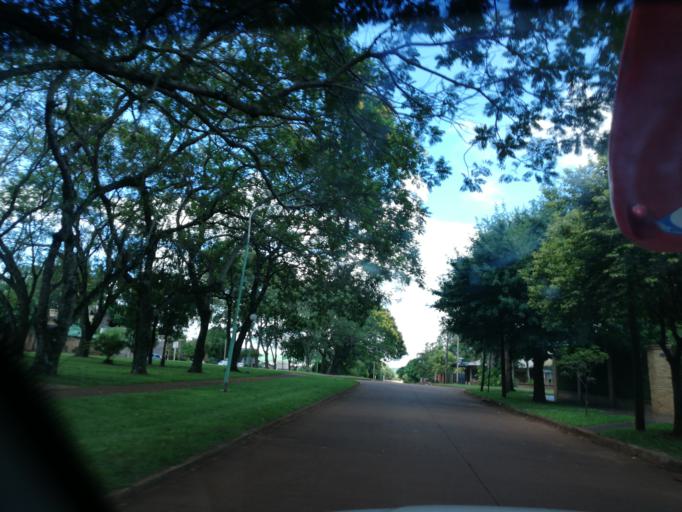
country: AR
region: Misiones
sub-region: Departamento de Apostoles
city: Apostoles
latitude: -27.9161
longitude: -55.7497
